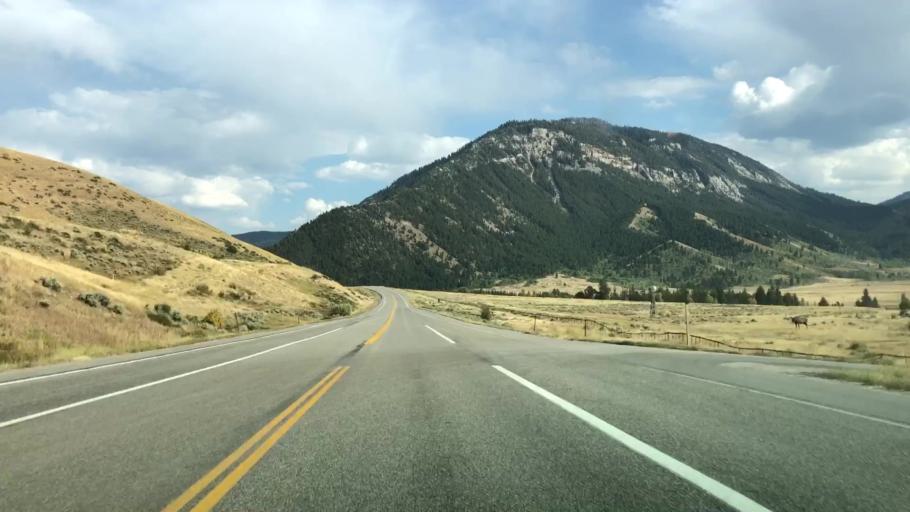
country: US
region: Wyoming
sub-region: Teton County
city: Hoback
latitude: 43.2936
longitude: -110.6561
